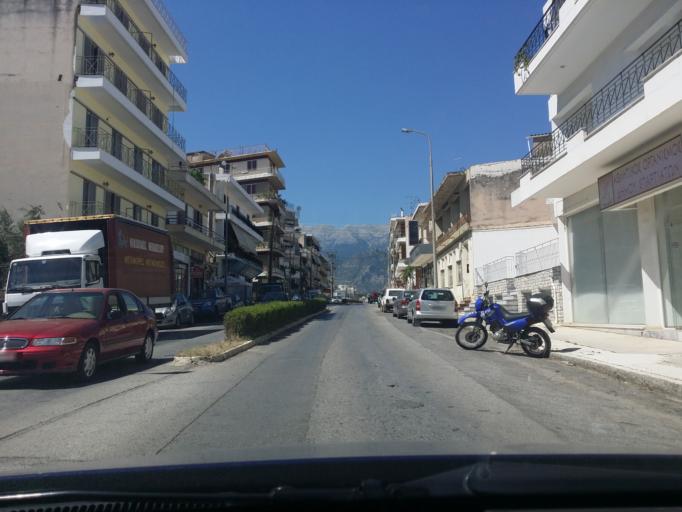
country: GR
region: Peloponnese
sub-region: Nomos Lakonias
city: Sparti
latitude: 37.0797
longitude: 22.4324
